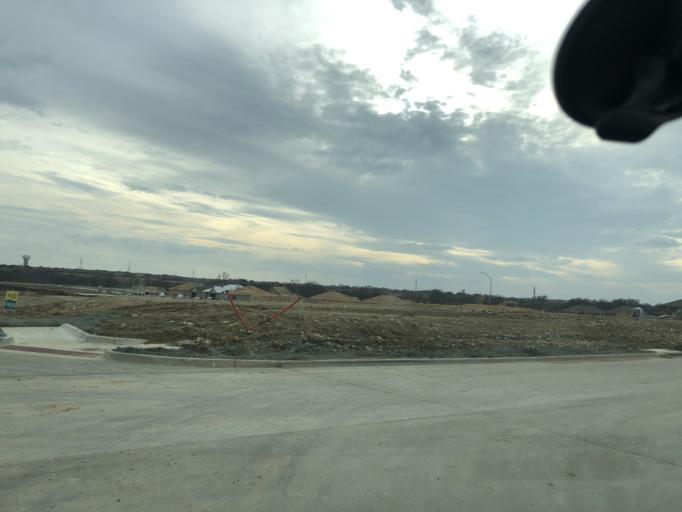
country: US
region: Texas
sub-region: Tarrant County
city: Saginaw
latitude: 32.9030
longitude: -97.3644
